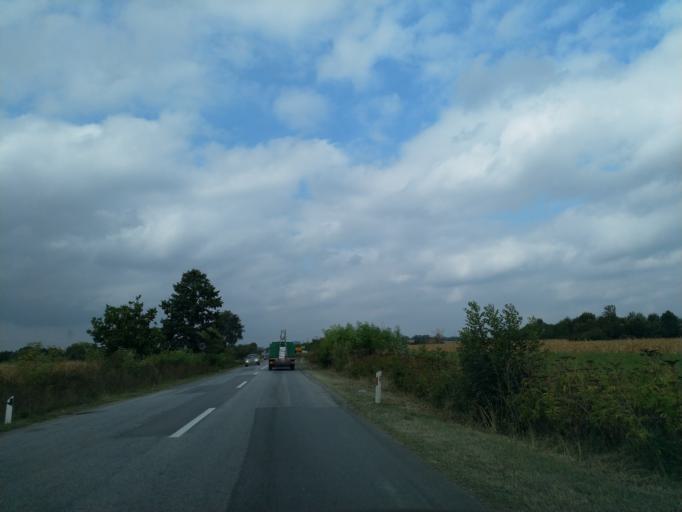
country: RS
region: Central Serbia
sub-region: Sumadijski Okrug
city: Kragujevac
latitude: 44.1126
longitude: 20.8392
